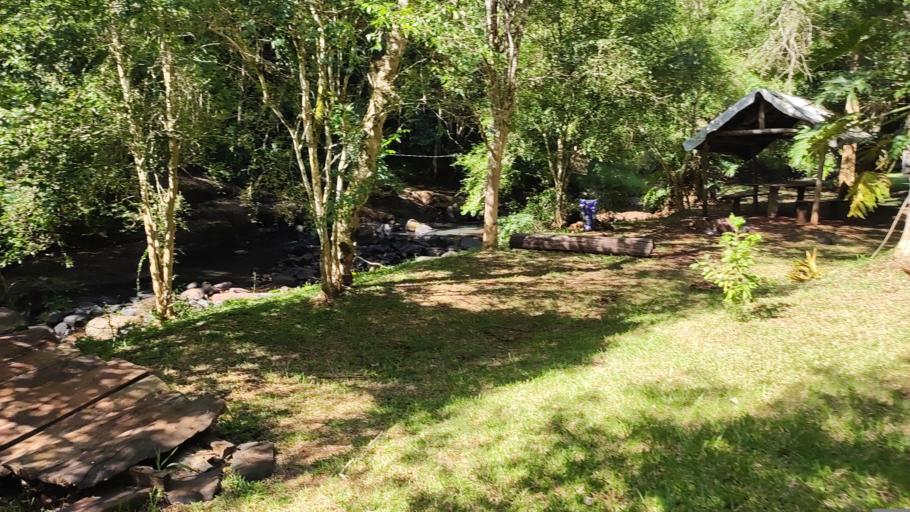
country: AR
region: Misiones
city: Capiovi
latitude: -26.9311
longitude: -55.0751
